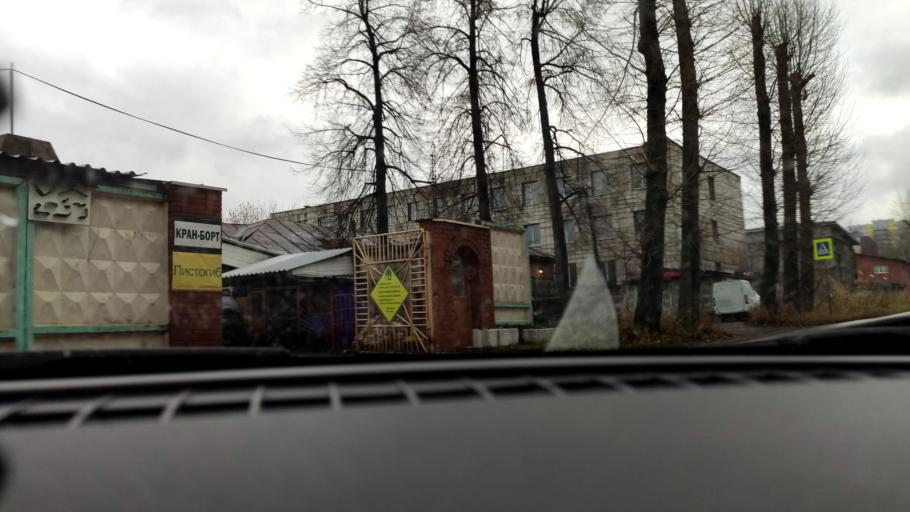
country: RU
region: Perm
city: Perm
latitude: 58.0967
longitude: 56.3705
